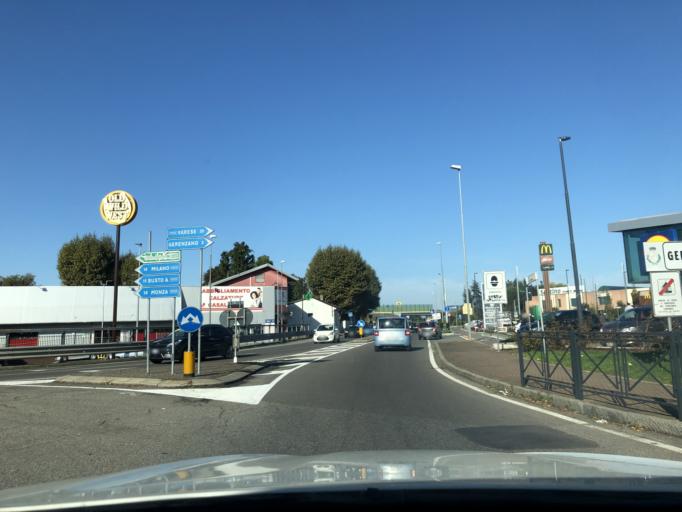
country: IT
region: Lombardy
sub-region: Provincia di Varese
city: Gerenzano
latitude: 45.6319
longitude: 9.0171
